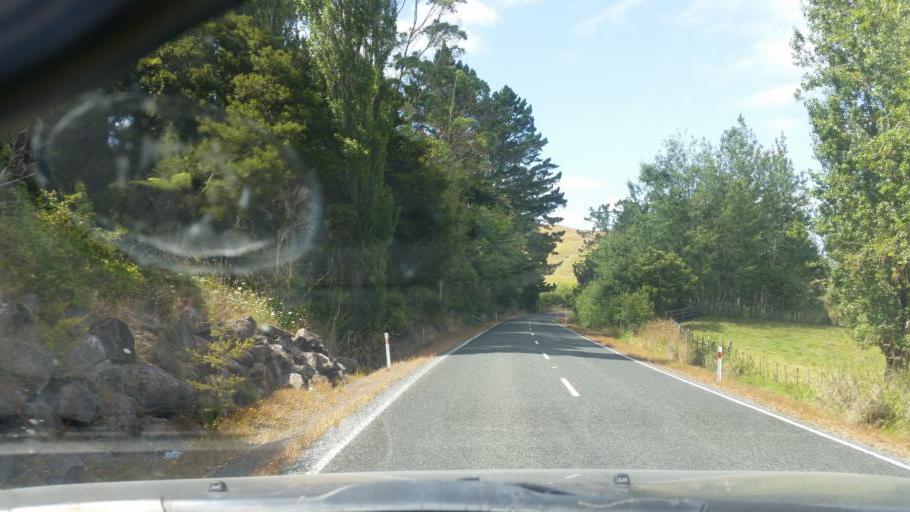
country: NZ
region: Northland
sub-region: Whangarei
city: Ruakaka
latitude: -35.9475
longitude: 174.2932
